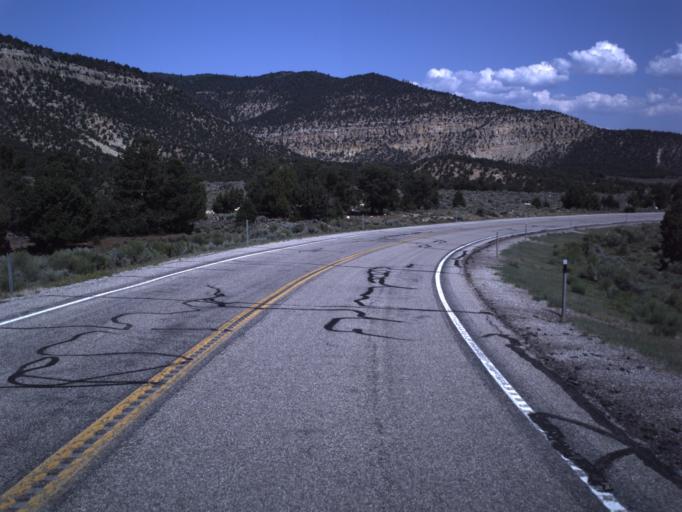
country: US
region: Utah
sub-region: Wayne County
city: Loa
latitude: 38.7028
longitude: -111.4018
